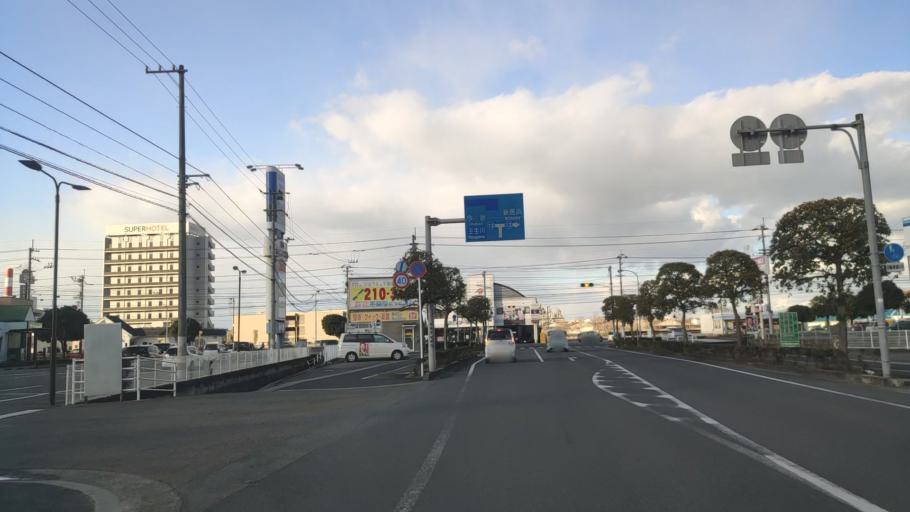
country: JP
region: Ehime
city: Saijo
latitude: 33.9273
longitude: 133.1834
